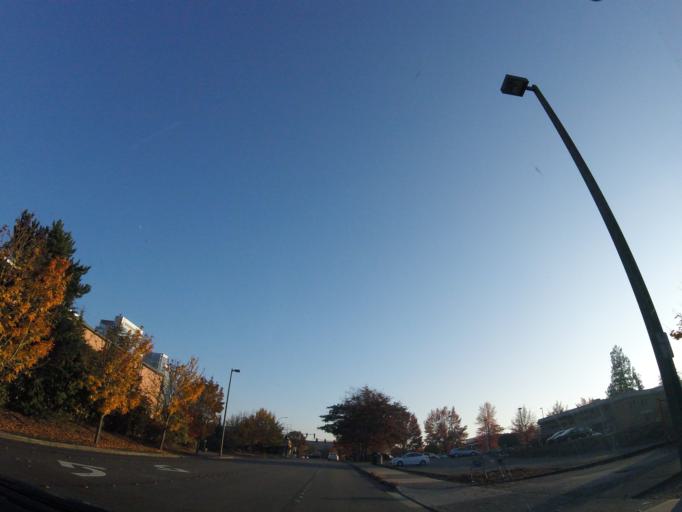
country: US
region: Washington
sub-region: King County
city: Bellevue
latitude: 47.6204
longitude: -122.2044
